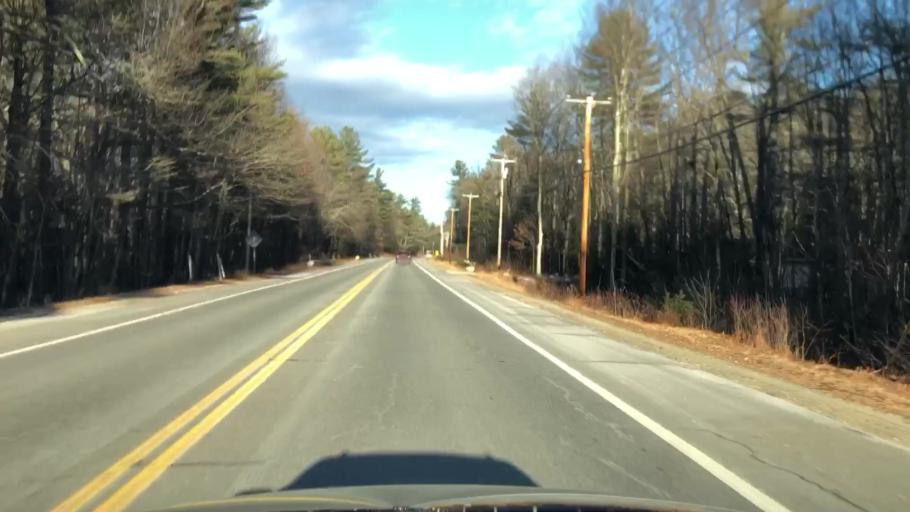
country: US
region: New Hampshire
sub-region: Hillsborough County
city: Brookline
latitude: 42.7795
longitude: -71.6646
